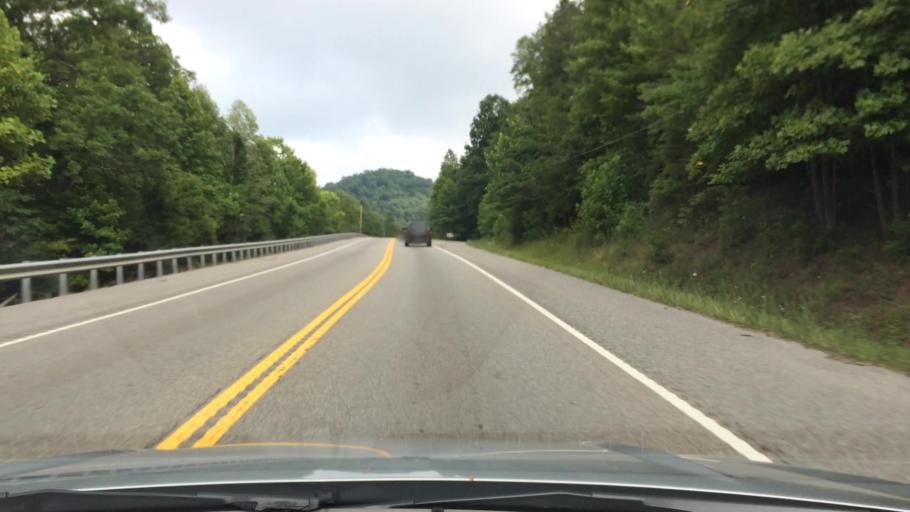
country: US
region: Tennessee
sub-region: Campbell County
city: Caryville
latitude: 36.4100
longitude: -84.2955
